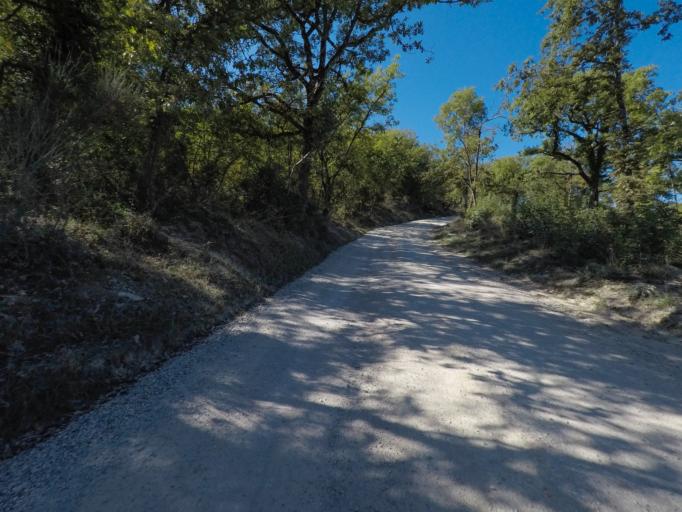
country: IT
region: Tuscany
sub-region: Provincia di Siena
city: Castellina in Chianti
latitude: 43.4356
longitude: 11.3214
